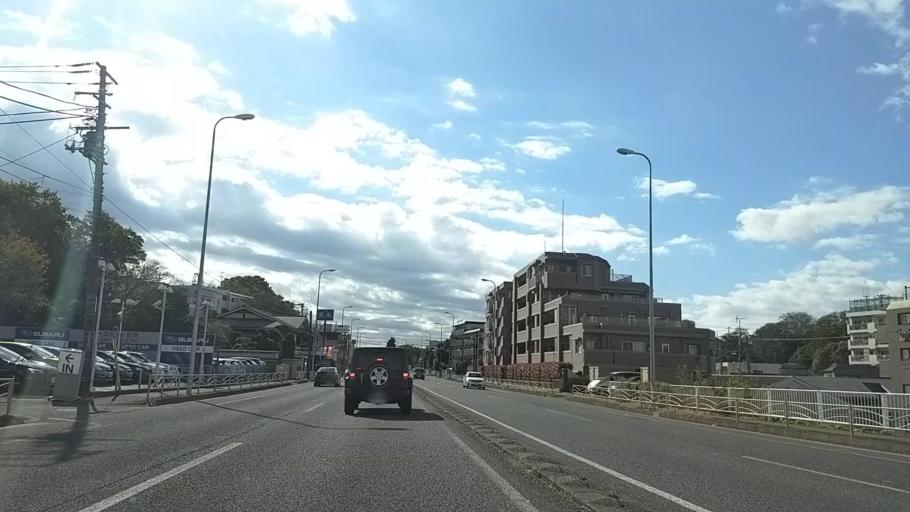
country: JP
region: Kanagawa
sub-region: Kawasaki-shi
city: Kawasaki
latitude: 35.5103
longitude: 139.6626
